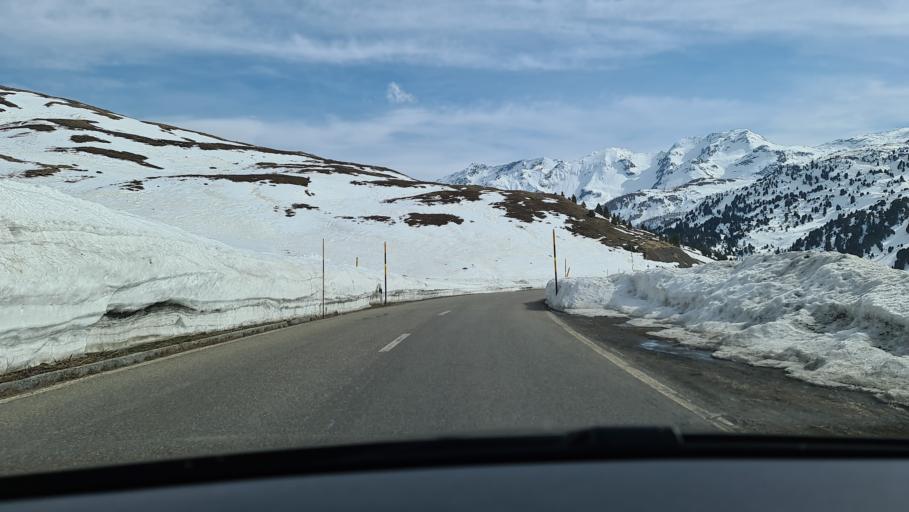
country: CH
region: Ticino
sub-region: Leventina District
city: Faido
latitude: 46.5601
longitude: 8.8014
